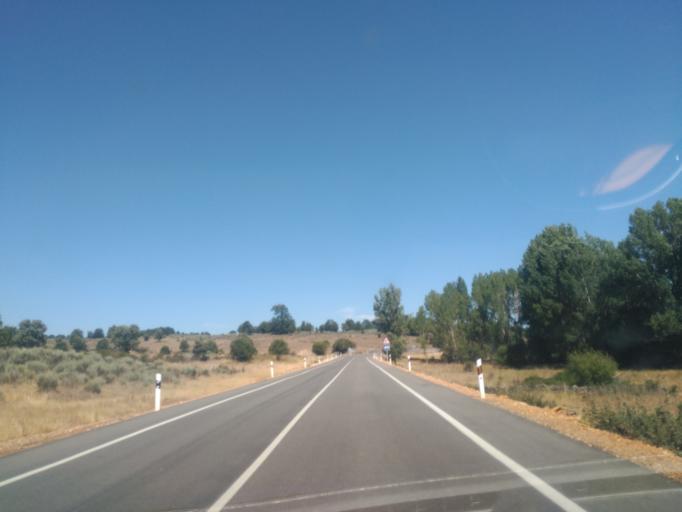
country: ES
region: Castille and Leon
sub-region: Provincia de Zamora
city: Ferreras de Arriba
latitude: 41.9605
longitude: -6.2172
